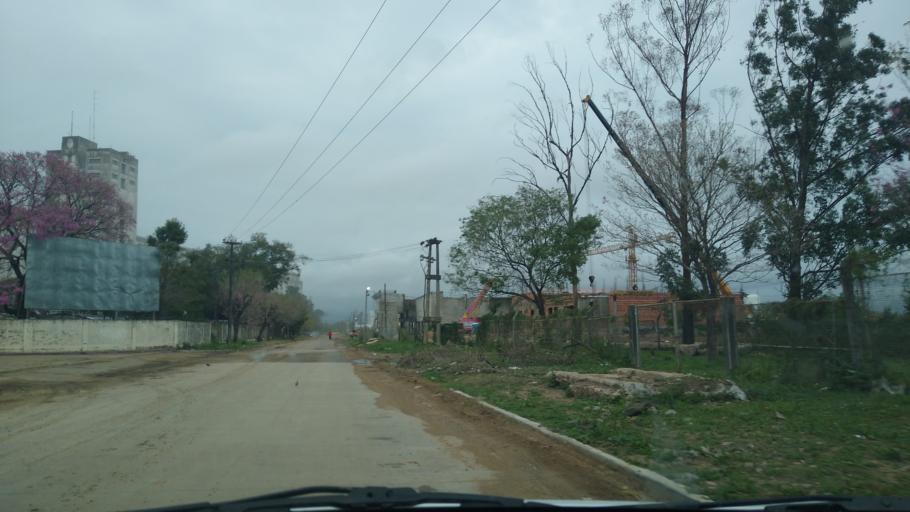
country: AR
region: Chaco
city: Barranqueras
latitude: -27.4710
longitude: -58.9088
